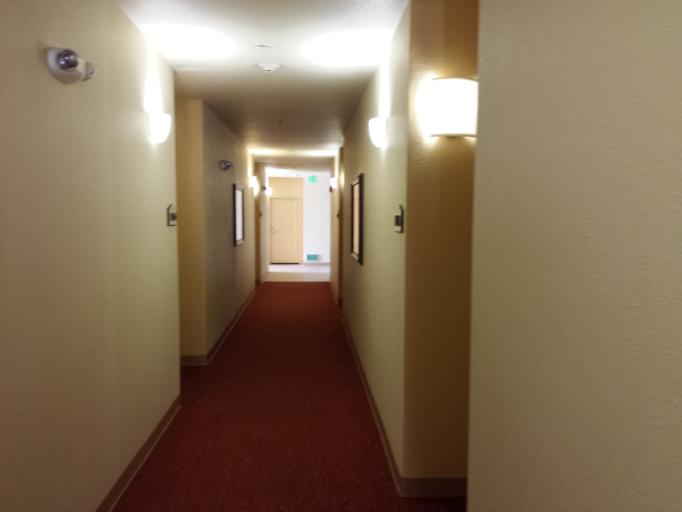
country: US
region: California
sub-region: San Luis Obispo County
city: Grover Beach
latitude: 35.1220
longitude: -120.6073
